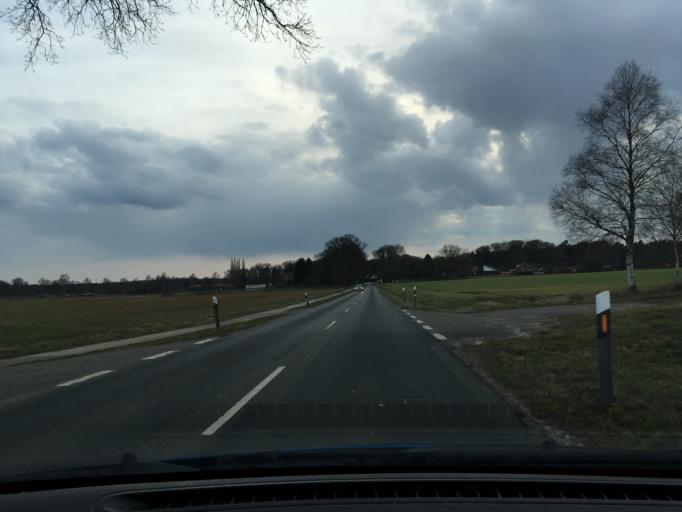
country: DE
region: Lower Saxony
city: Reppenstedt
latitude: 53.2563
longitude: 10.3253
